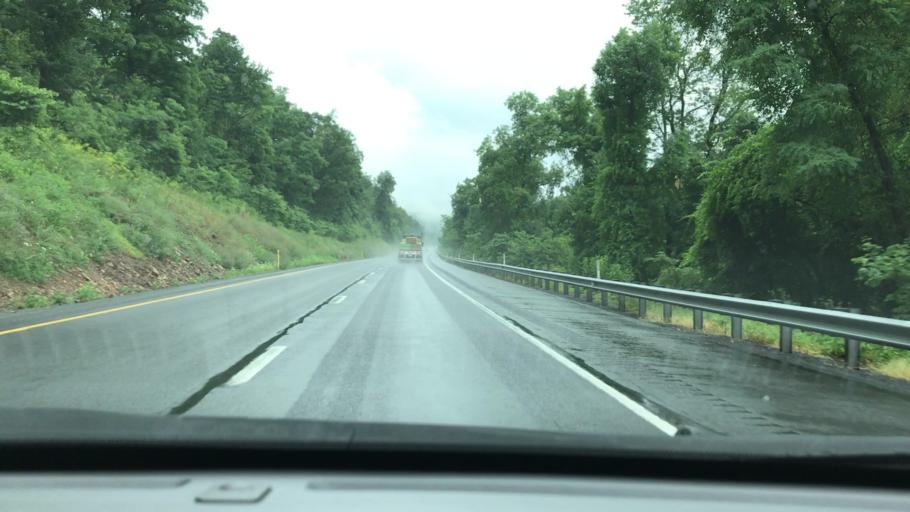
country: US
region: Maryland
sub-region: Washington County
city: Hancock
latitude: 39.8499
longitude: -78.2718
